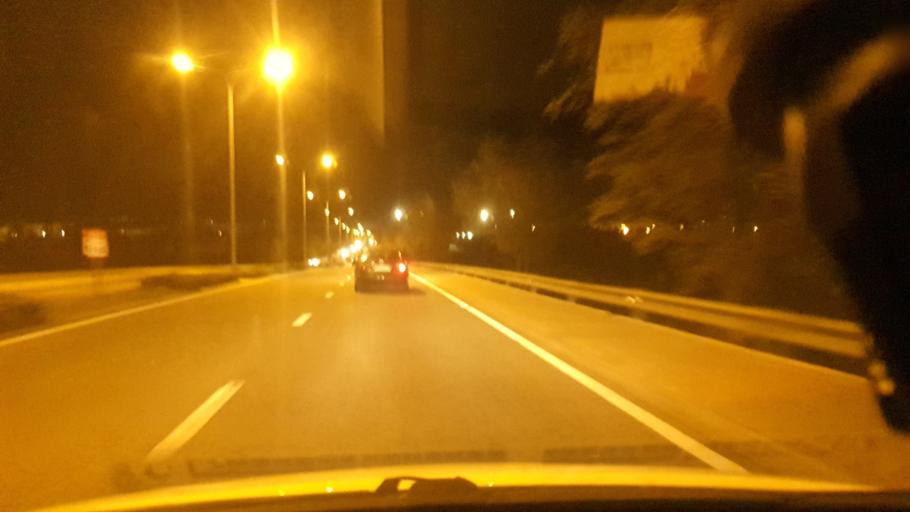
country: ES
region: Castille and Leon
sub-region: Provincia de Avila
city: Avila
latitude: 40.6514
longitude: -4.7102
